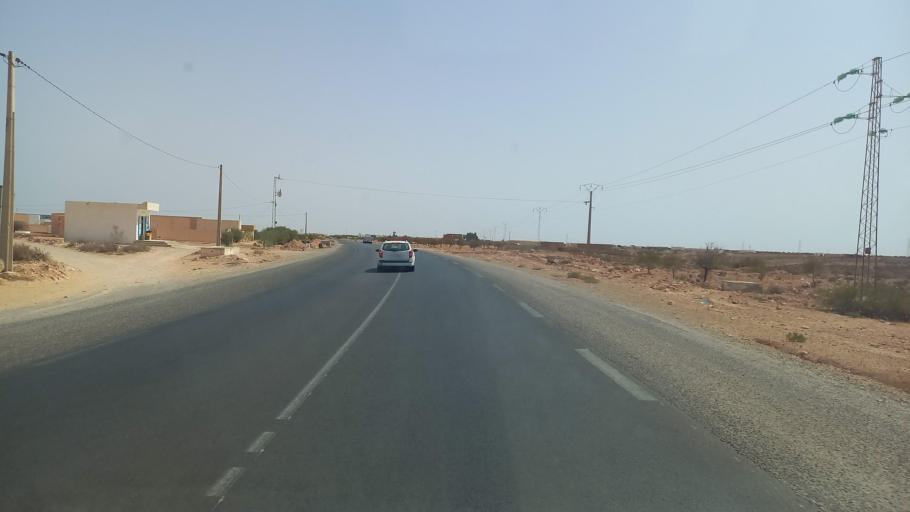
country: TN
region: Madanin
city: Medenine
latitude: 33.3676
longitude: 10.6689
